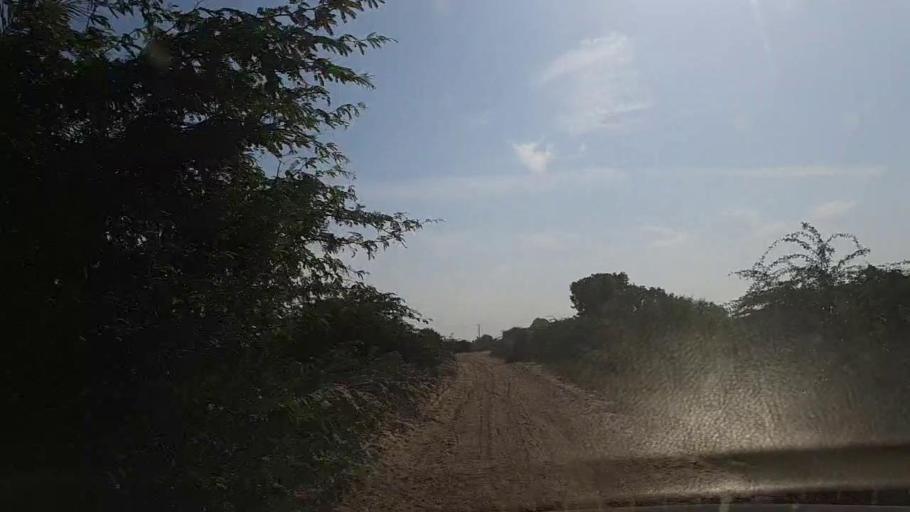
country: PK
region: Sindh
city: Bulri
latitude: 24.8377
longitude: 68.2815
